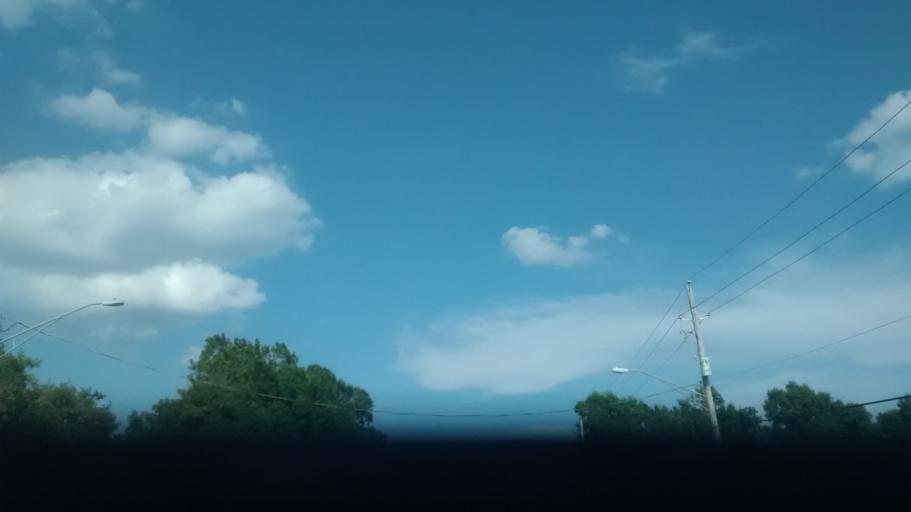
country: US
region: Arkansas
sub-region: Washington County
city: Fayetteville
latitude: 36.0781
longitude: -94.1953
